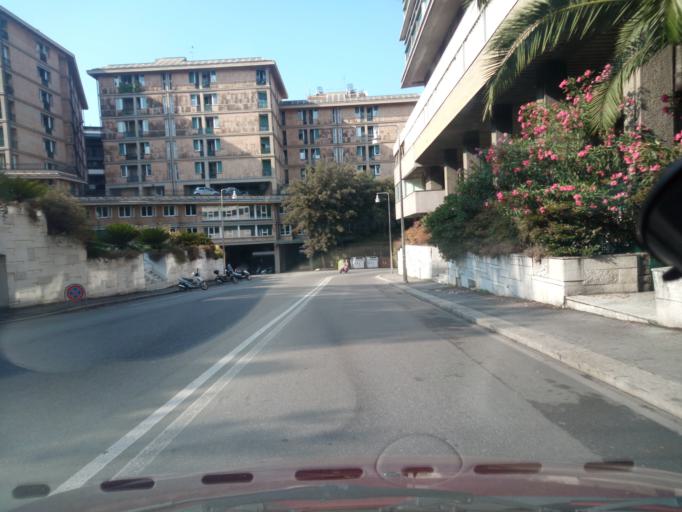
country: IT
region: Liguria
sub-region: Provincia di Genova
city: Genoa
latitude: 44.4092
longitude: 8.9386
